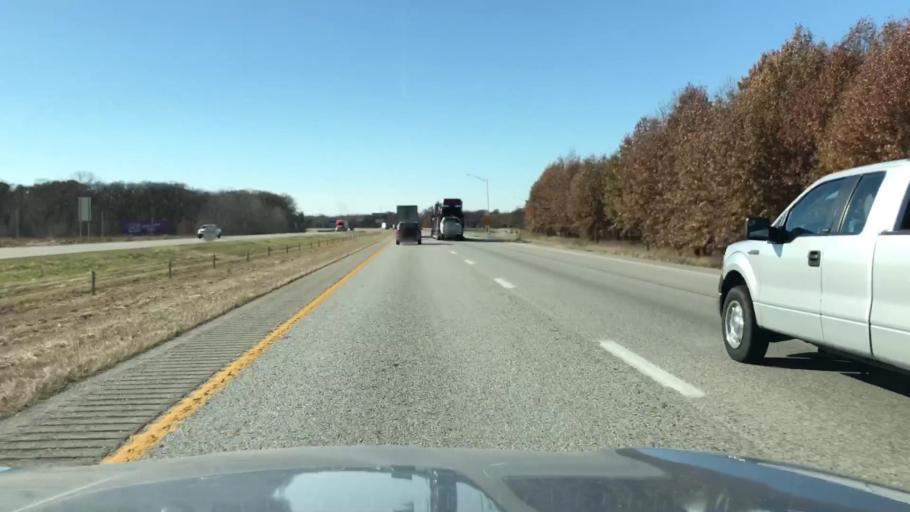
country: US
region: Missouri
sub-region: Jasper County
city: Duenweg
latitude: 37.0822
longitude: -94.3584
